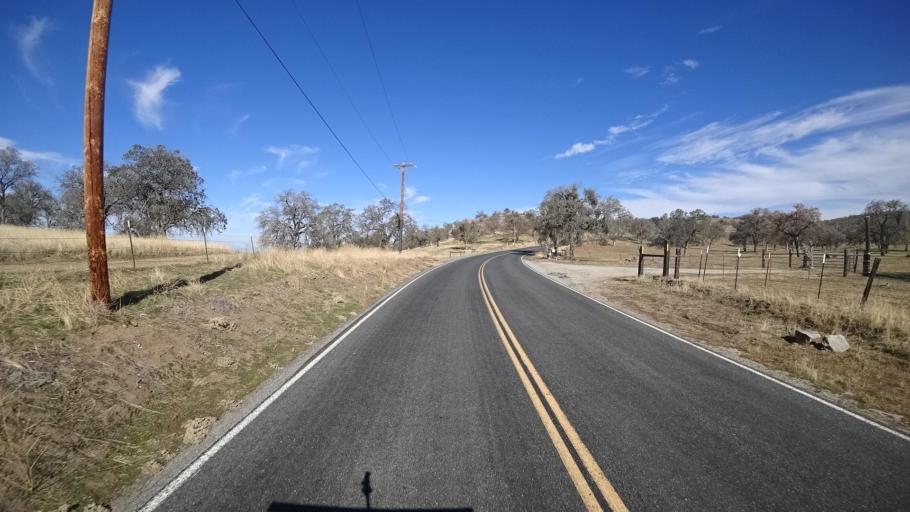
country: US
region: California
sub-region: Kern County
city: Alta Sierra
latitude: 35.6419
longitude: -118.7998
